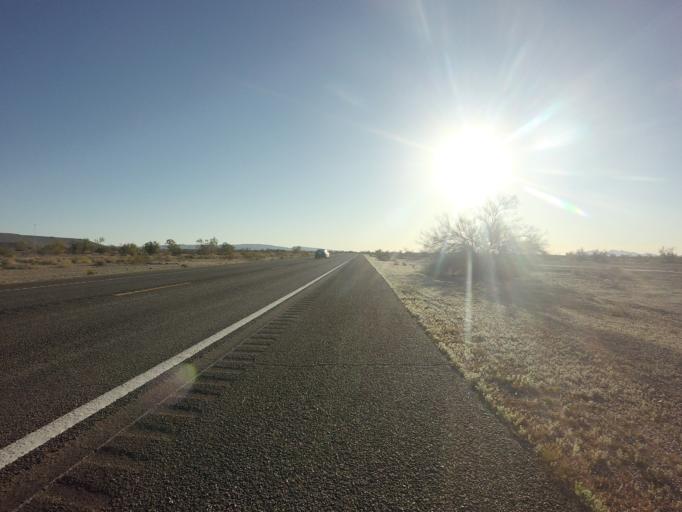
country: MX
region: Baja California
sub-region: Mexicali
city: Ejido Netzahualcoyotl
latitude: 33.0150
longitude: -114.9999
